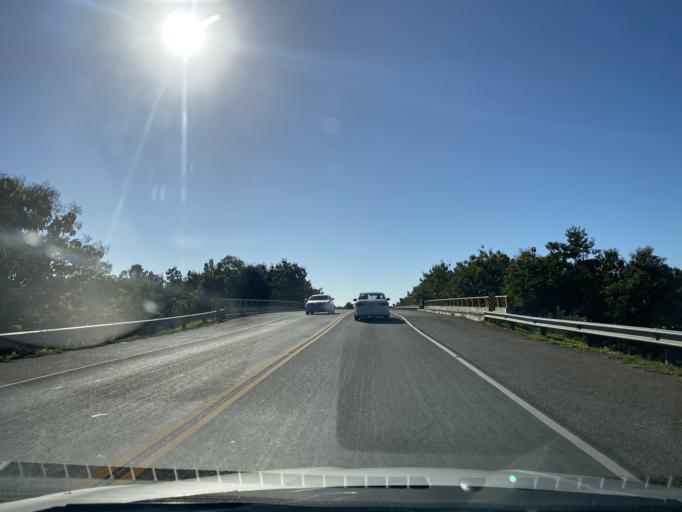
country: DO
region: Santo Domingo
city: Guerra
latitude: 18.5275
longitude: -69.7501
